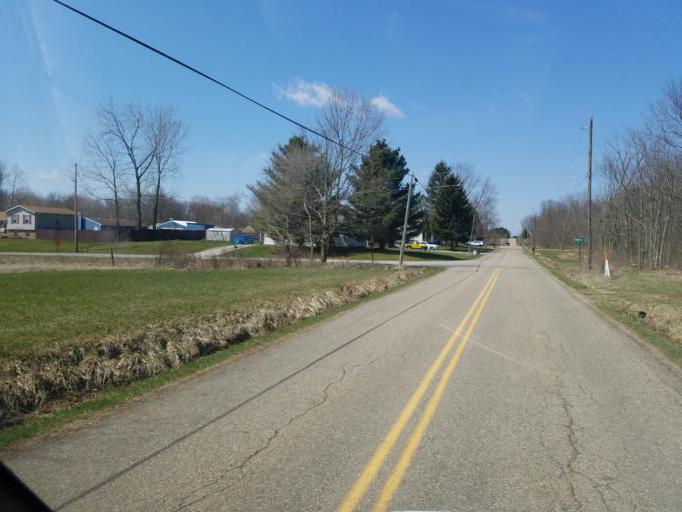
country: US
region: Ohio
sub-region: Knox County
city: Centerburg
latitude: 40.2959
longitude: -82.6789
